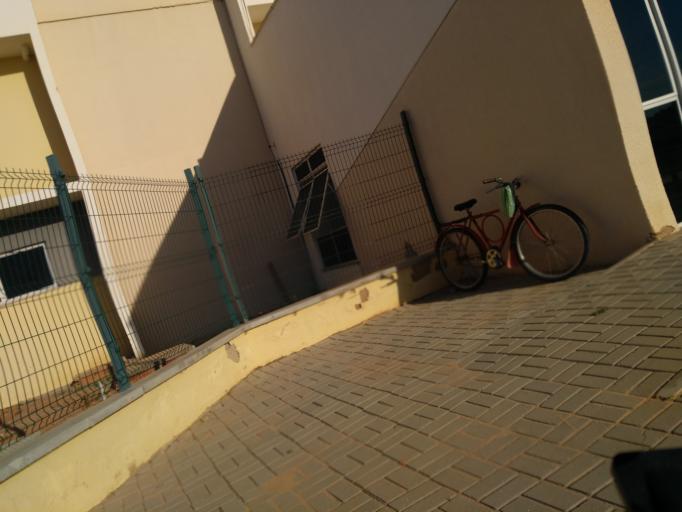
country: BR
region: Ceara
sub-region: Aracati
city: Aracati
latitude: -4.5671
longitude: -37.7915
